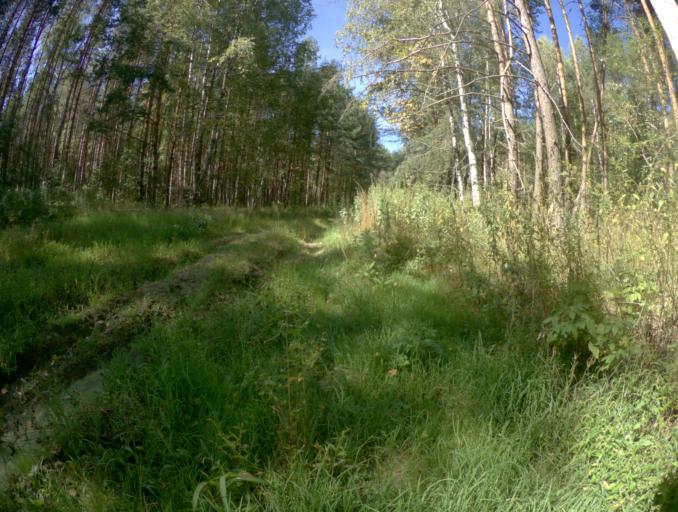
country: RU
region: Vladimir
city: Dobryatino
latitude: 55.6375
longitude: 41.3181
